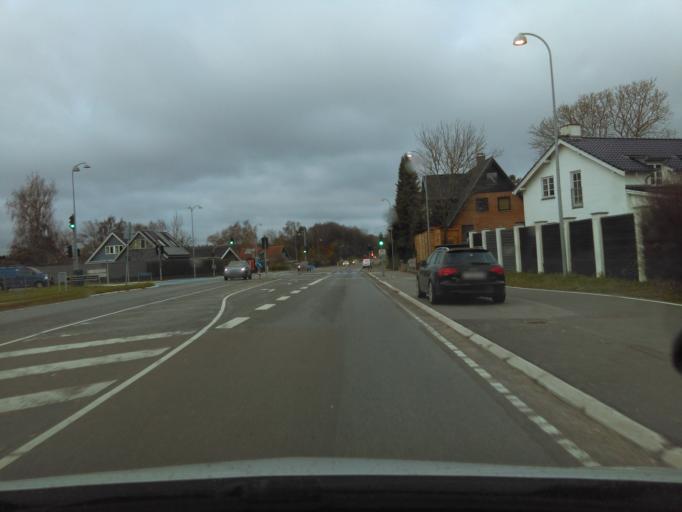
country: DK
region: Capital Region
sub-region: Fureso Kommune
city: Vaerlose
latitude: 55.7651
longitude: 12.3661
